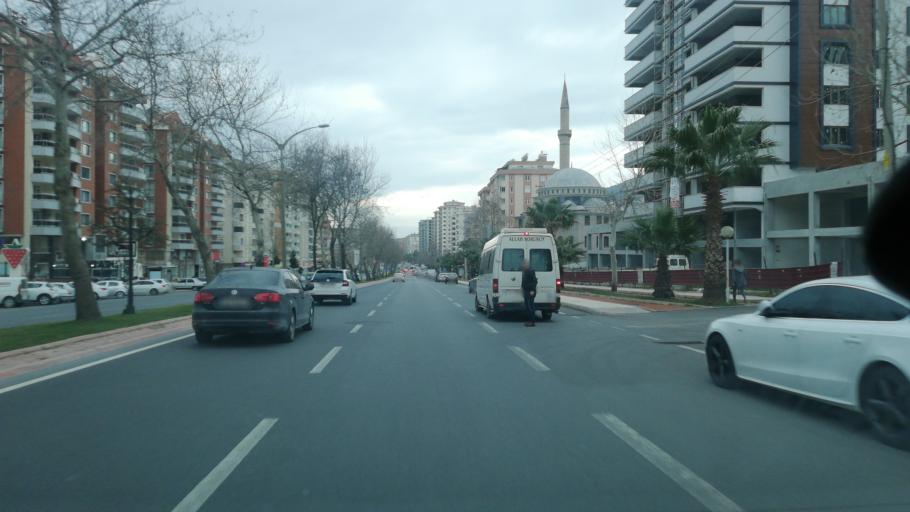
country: TR
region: Kahramanmaras
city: Kahramanmaras
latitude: 37.5905
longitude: 36.8729
